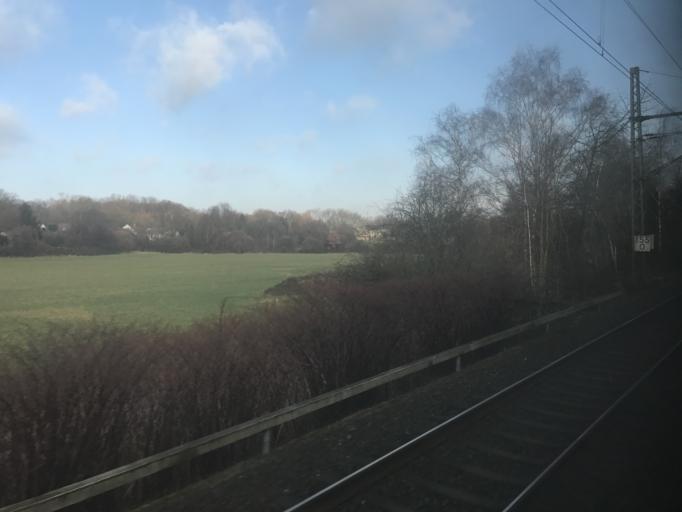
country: DE
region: North Rhine-Westphalia
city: Witten
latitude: 51.4864
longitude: 7.3423
